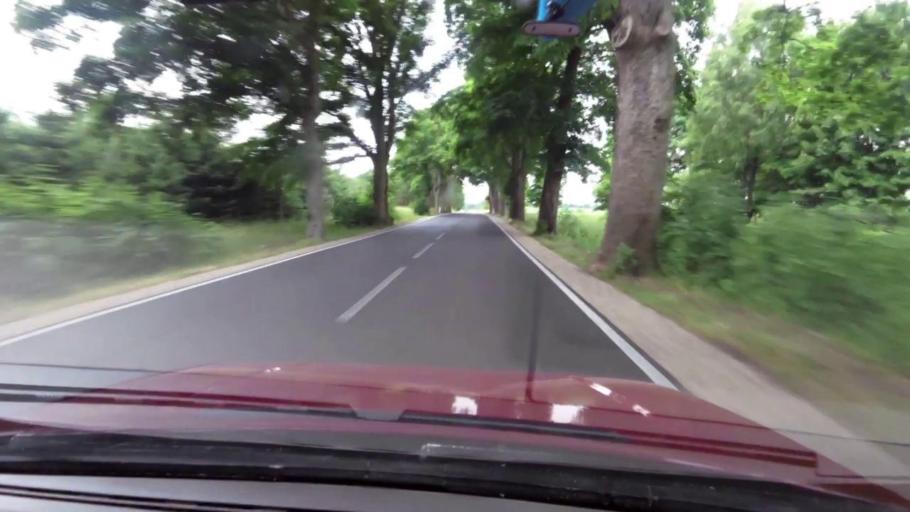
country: PL
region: West Pomeranian Voivodeship
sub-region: Powiat koszalinski
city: Sianow
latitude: 54.1569
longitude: 16.4578
